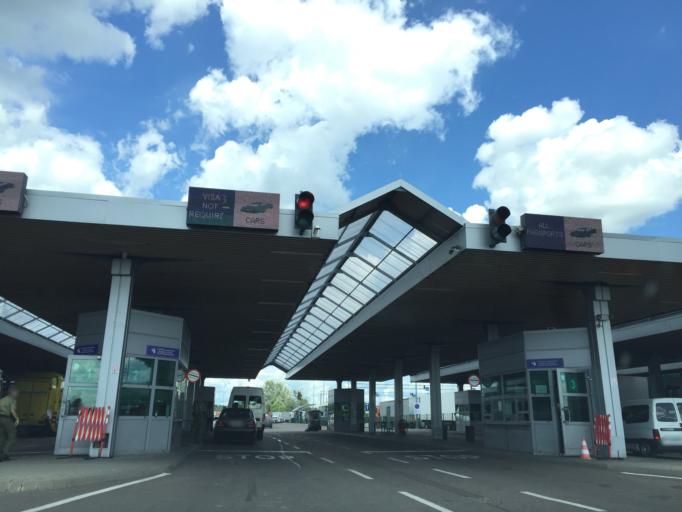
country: PL
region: Lublin Voivodeship
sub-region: Powiat chelmski
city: Dorohusk
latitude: 51.1804
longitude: 23.8026
